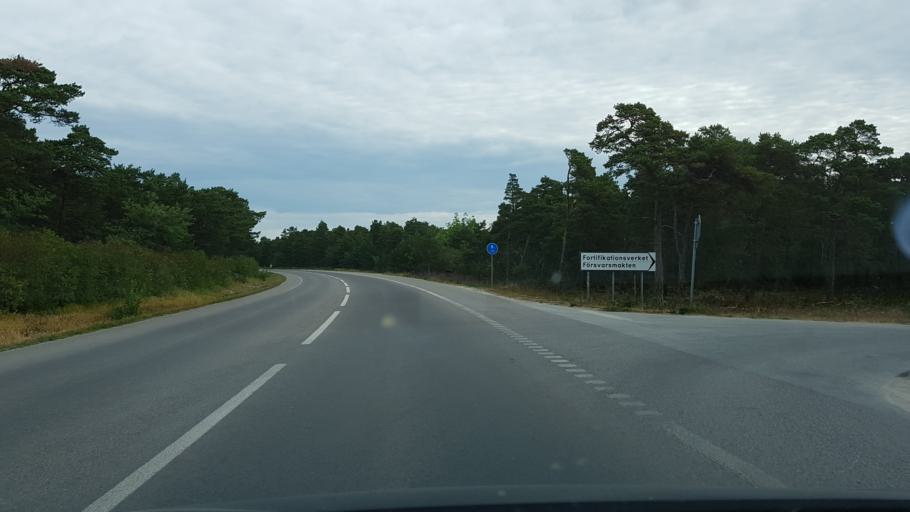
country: SE
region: Gotland
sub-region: Gotland
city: Visby
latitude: 57.6738
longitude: 18.3416
